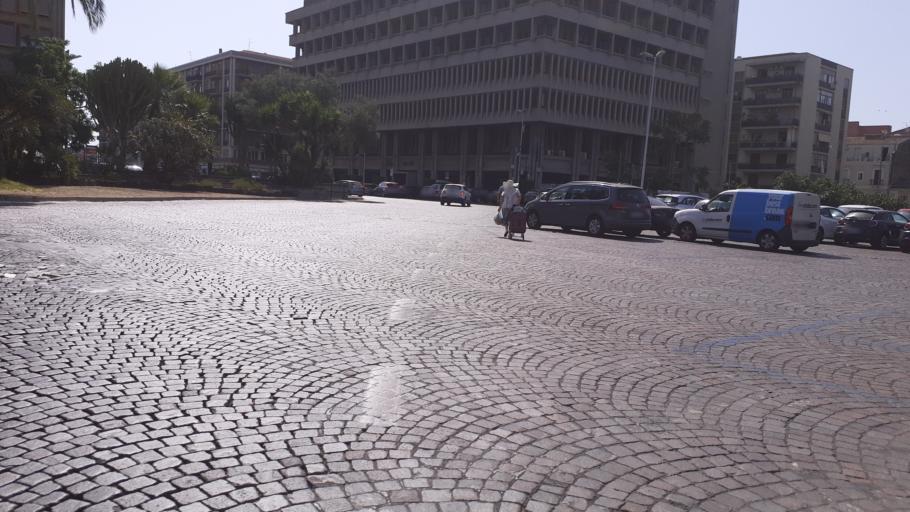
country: IT
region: Sicily
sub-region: Catania
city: Catania
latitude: 37.5077
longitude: 15.0914
